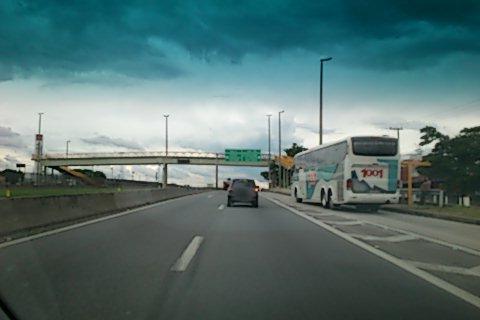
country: BR
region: Sao Paulo
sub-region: Sao Jose Dos Campos
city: Sao Jose dos Campos
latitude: -23.2145
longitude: -45.8945
